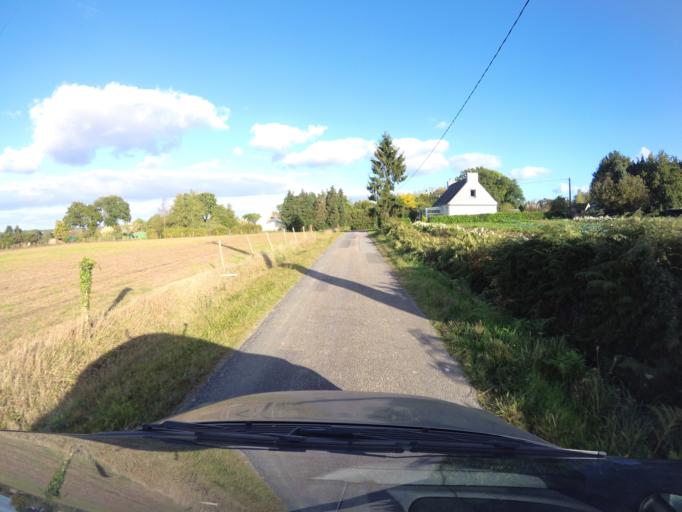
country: FR
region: Brittany
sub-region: Departement du Morbihan
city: Saint-Vincent-sur-Oust
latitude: 47.7143
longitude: -2.1753
